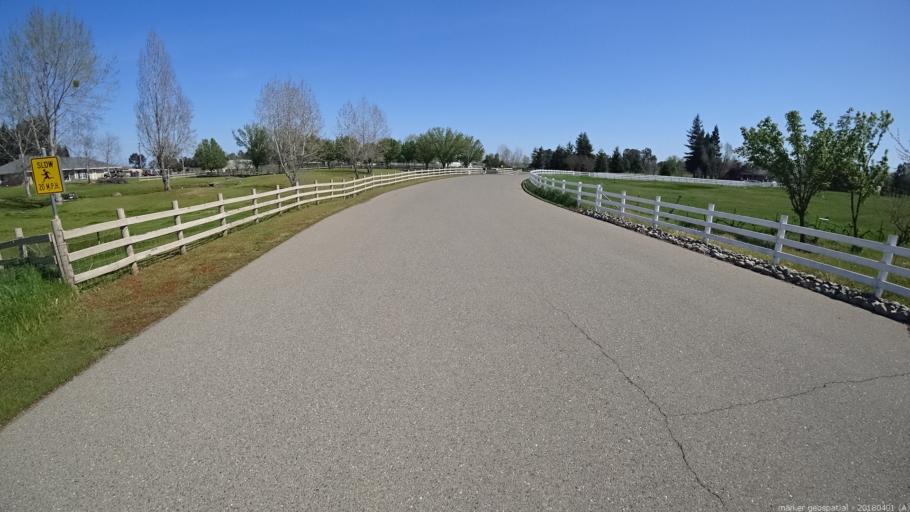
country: US
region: California
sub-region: Sacramento County
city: Wilton
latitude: 38.4073
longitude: -121.2165
